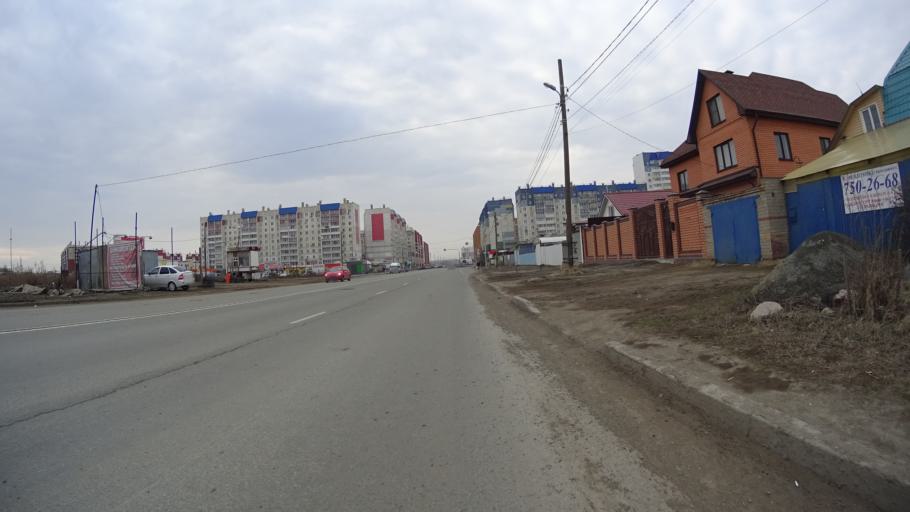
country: RU
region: Chelyabinsk
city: Zheleznodorozhnyy
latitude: 55.1651
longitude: 61.5223
